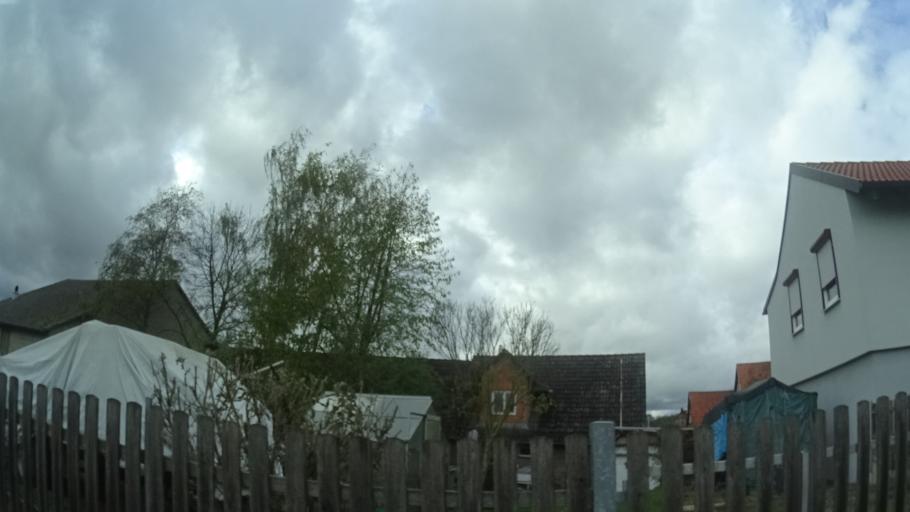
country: DE
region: Bavaria
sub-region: Regierungsbezirk Unterfranken
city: Wuelfershausen
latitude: 50.3319
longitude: 10.3424
